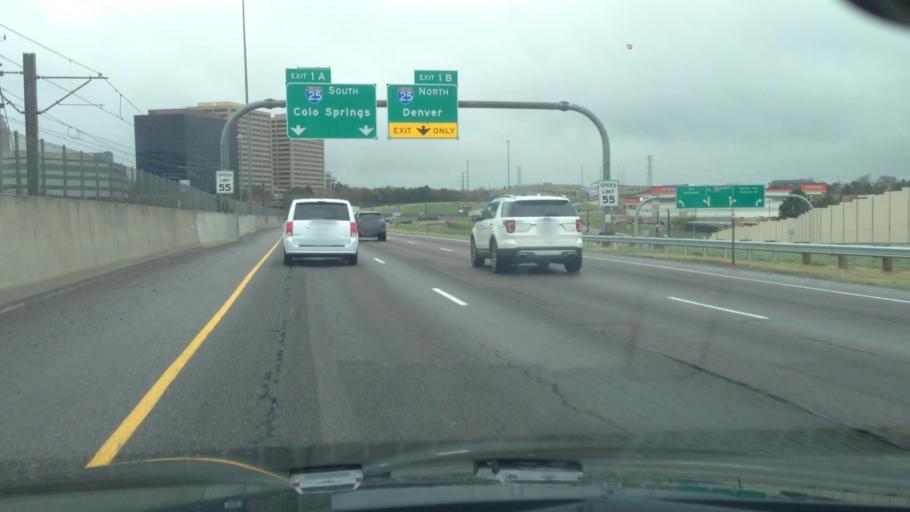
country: US
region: Colorado
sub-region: Arapahoe County
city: Castlewood
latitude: 39.6370
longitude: -104.8903
